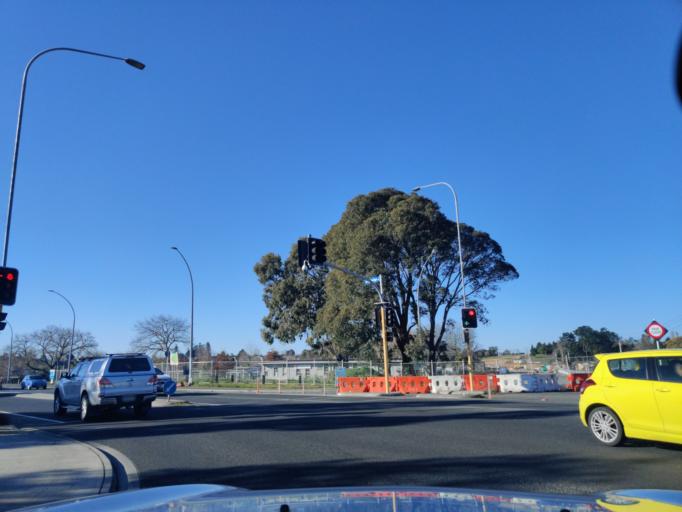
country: NZ
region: Waikato
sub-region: Hamilton City
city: Hamilton
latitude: -37.7973
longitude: 175.3082
